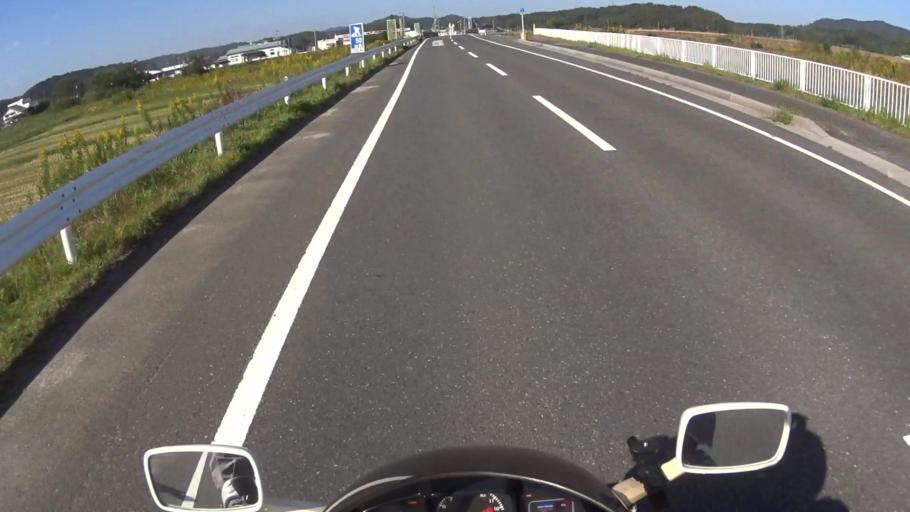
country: JP
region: Kyoto
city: Miyazu
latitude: 35.6697
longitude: 135.0895
